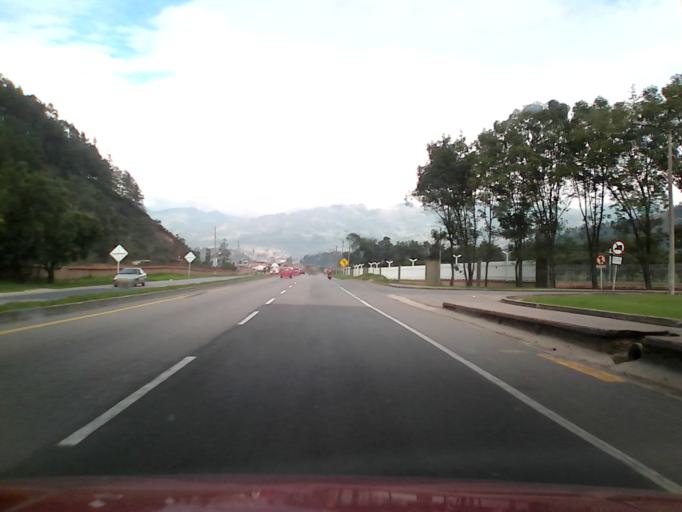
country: CO
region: Boyaca
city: Duitama
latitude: 5.8054
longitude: -73.0074
